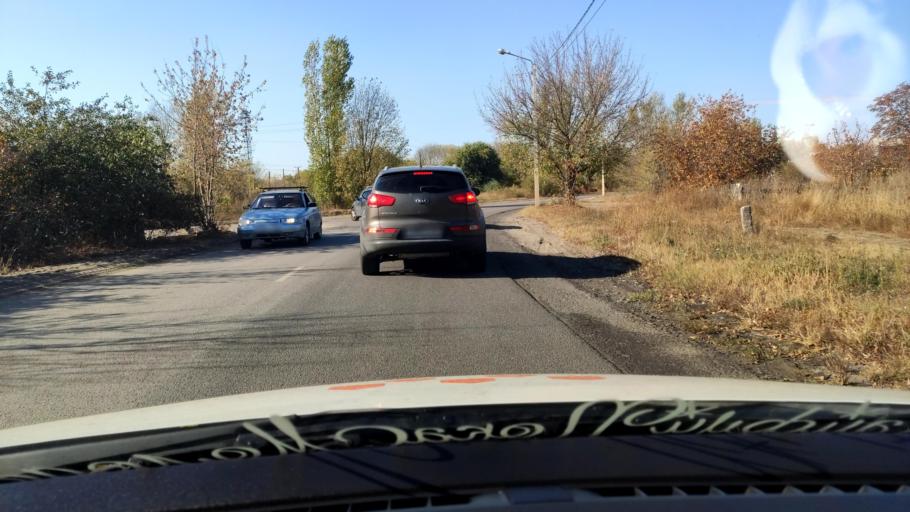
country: RU
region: Voronezj
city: Pridonskoy
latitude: 51.6836
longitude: 39.0679
